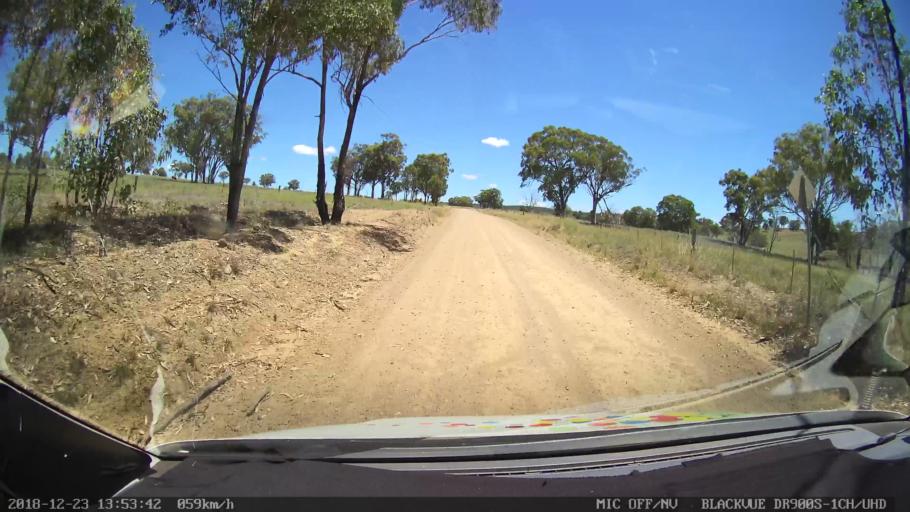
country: AU
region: New South Wales
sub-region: Tamworth Municipality
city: Manilla
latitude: -30.5546
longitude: 151.0927
